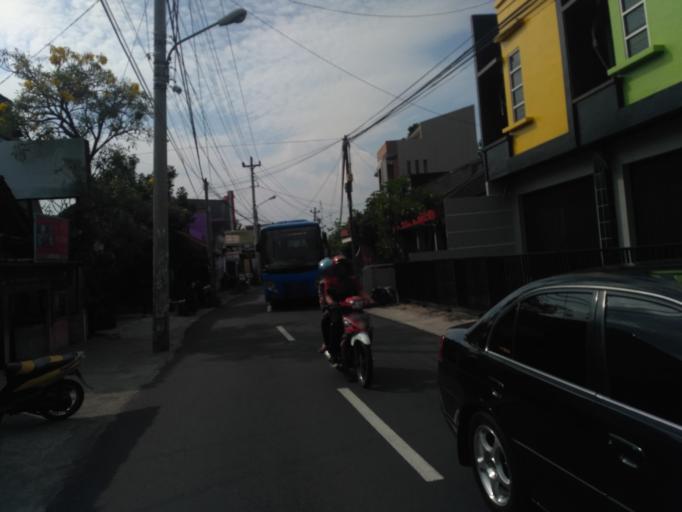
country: ID
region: Daerah Istimewa Yogyakarta
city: Depok
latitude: -7.7775
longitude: 110.4083
